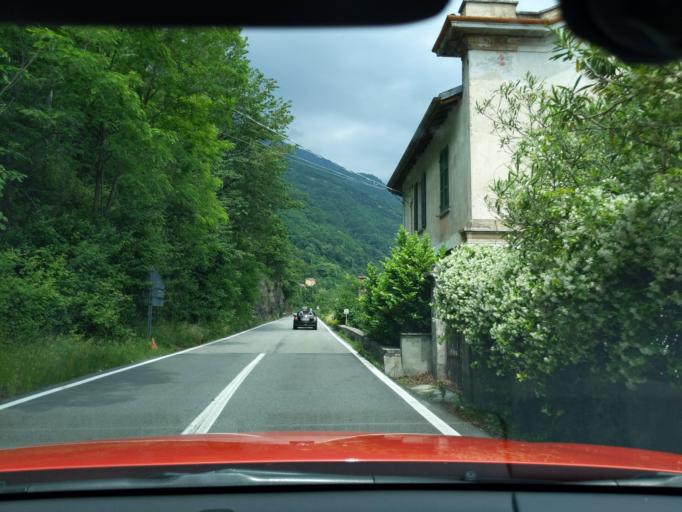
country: IT
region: Piedmont
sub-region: Provincia Verbano-Cusio-Ossola
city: Cannobio
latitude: 46.0827
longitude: 8.6930
